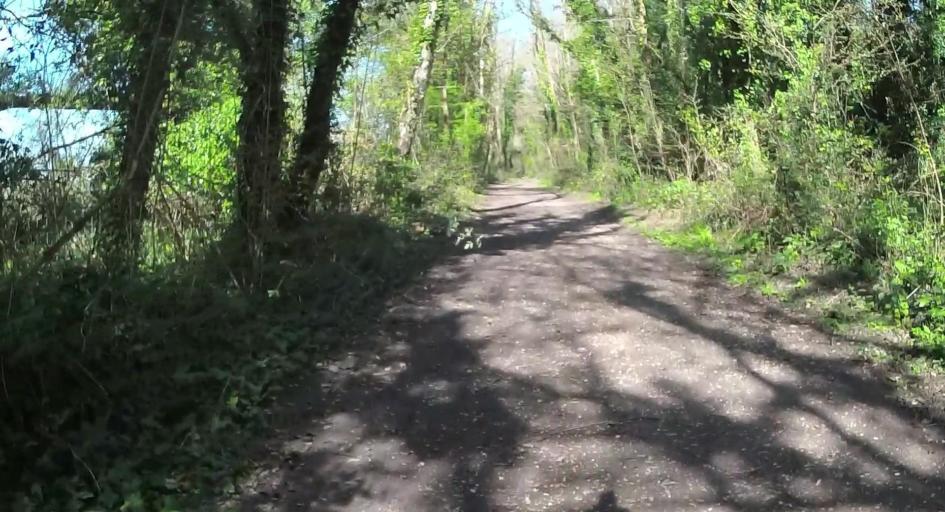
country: GB
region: England
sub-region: Hampshire
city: Romsey
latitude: 51.0769
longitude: -1.5053
